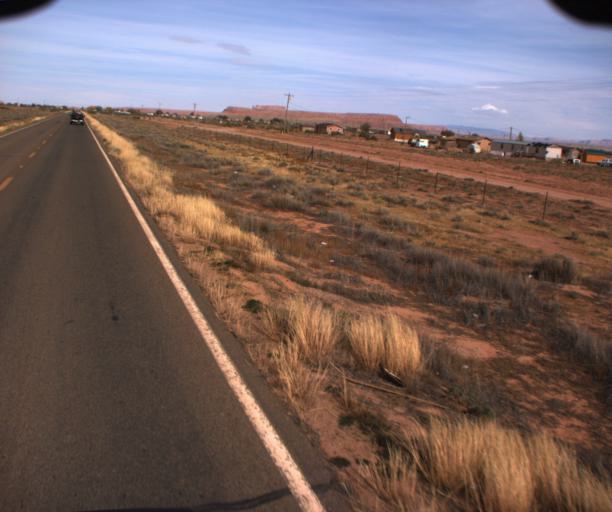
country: US
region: Arizona
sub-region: Apache County
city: Many Farms
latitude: 36.3970
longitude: -109.6094
